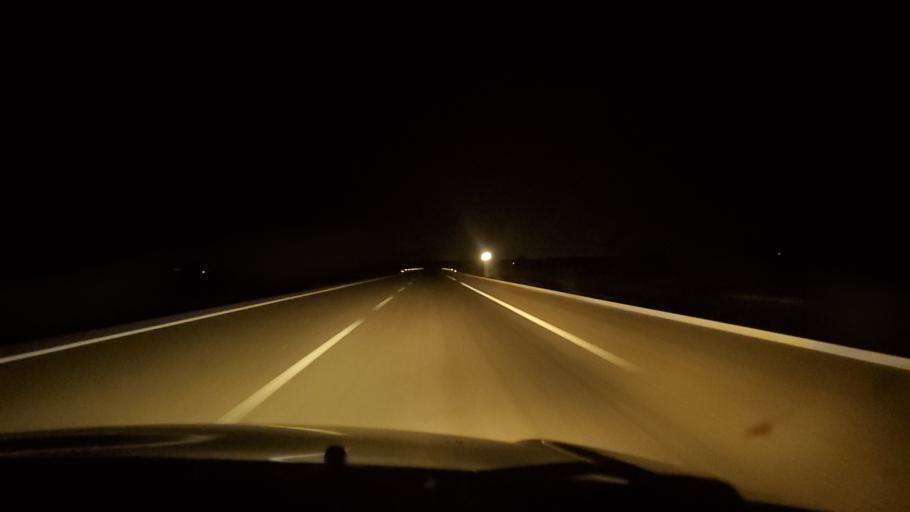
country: SN
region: Thies
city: Pout
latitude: 14.6982
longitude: -17.0260
